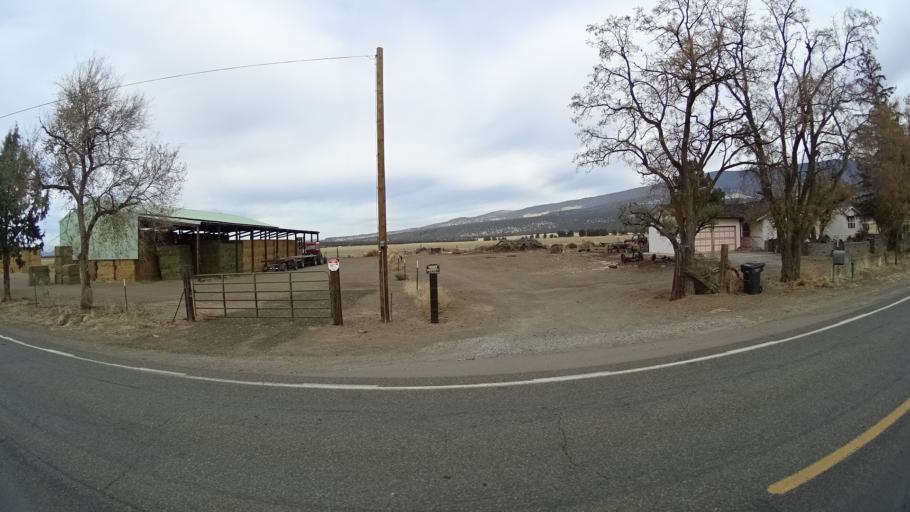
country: US
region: California
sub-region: Siskiyou County
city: Weed
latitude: 41.5948
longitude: -122.3253
